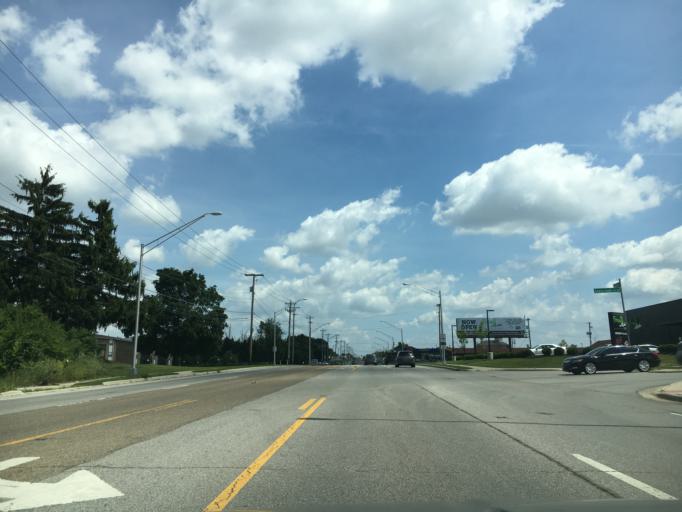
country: US
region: Ohio
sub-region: Franklin County
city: Lincoln Village
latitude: 39.9381
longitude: -83.1436
